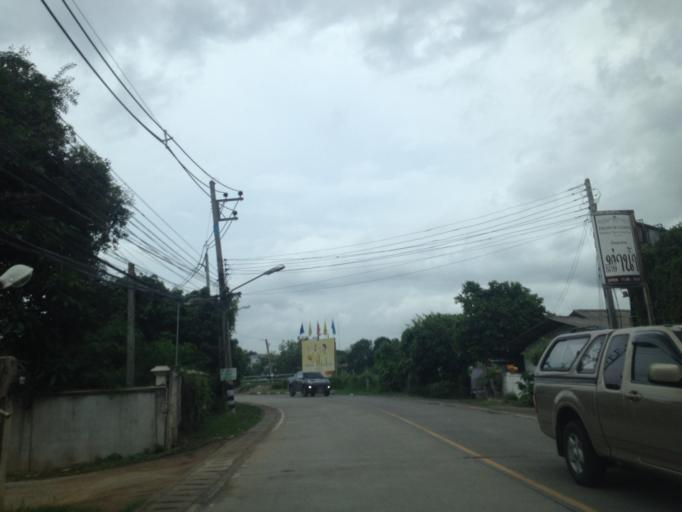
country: TH
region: Chiang Mai
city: Chiang Mai
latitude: 18.7558
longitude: 98.9945
